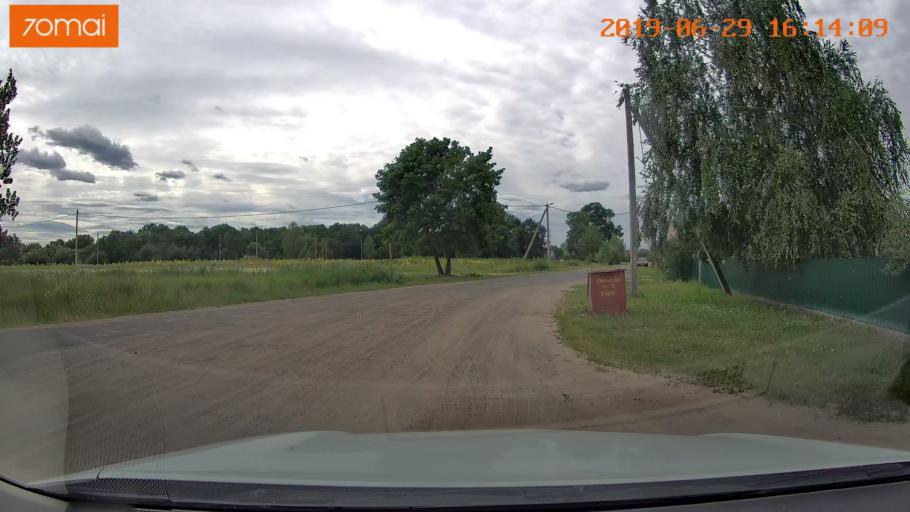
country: BY
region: Brest
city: Luninyets
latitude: 52.1994
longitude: 27.0171
